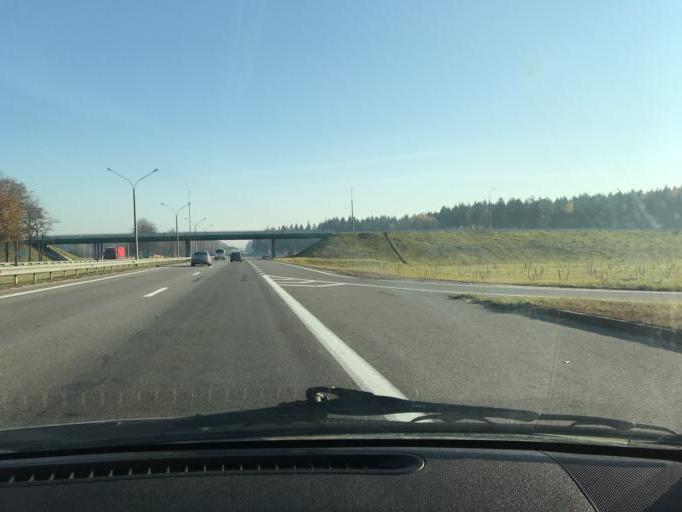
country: BY
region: Minsk
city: Korolev Stan
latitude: 53.9964
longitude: 27.8207
